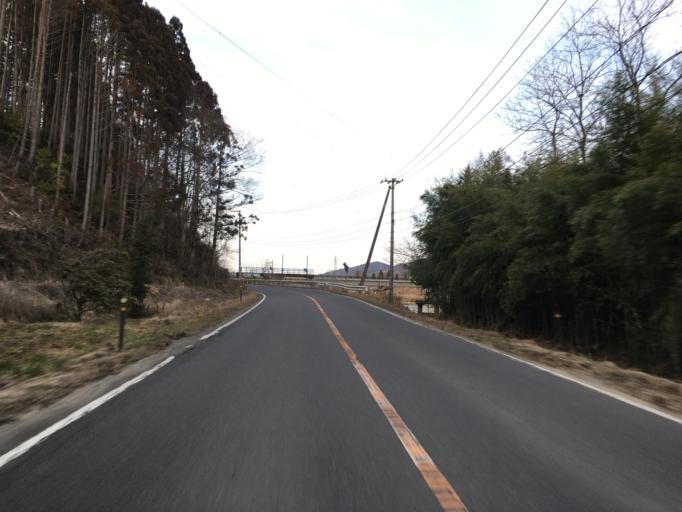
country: JP
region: Ibaraki
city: Daigo
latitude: 36.8925
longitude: 140.4114
